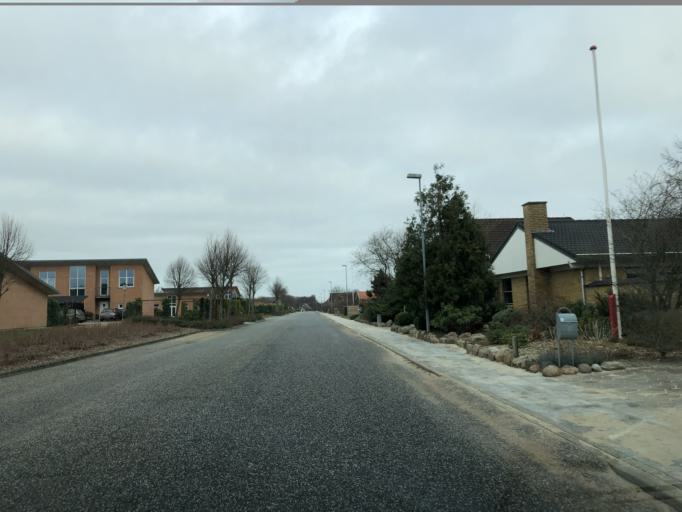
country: DK
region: Central Jutland
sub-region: Viborg Kommune
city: Stoholm
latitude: 56.4804
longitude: 9.1532
